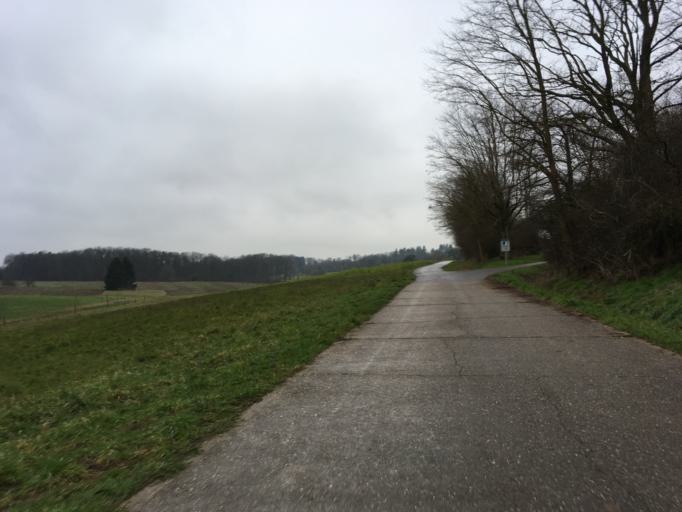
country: DE
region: Baden-Wuerttemberg
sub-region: Karlsruhe Region
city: Konigsbach-Stein
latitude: 48.9457
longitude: 8.5310
